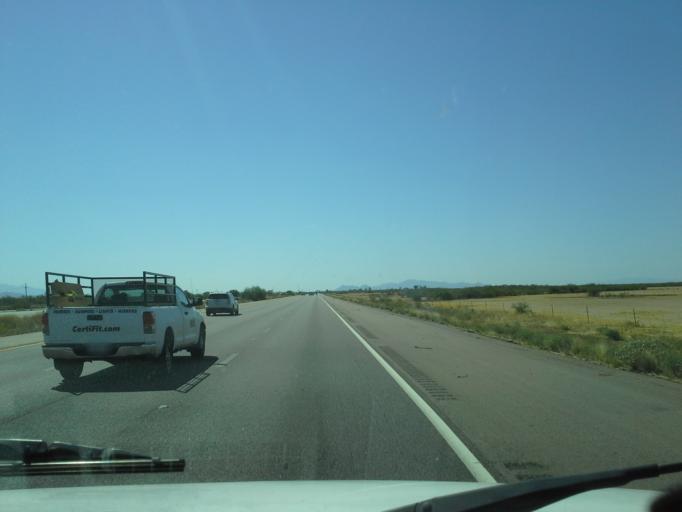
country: US
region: Arizona
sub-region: Pima County
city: Avra Valley
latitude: 32.6018
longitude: -111.3472
